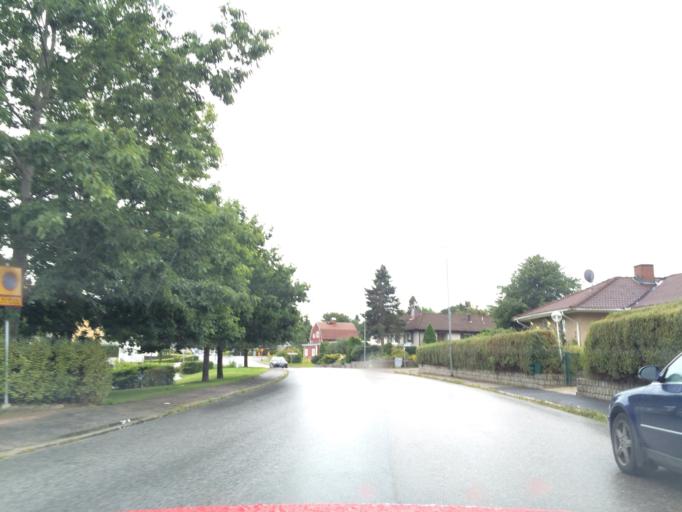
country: SE
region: Vaestra Goetaland
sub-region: Trollhattan
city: Trollhattan
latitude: 58.2846
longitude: 12.2607
